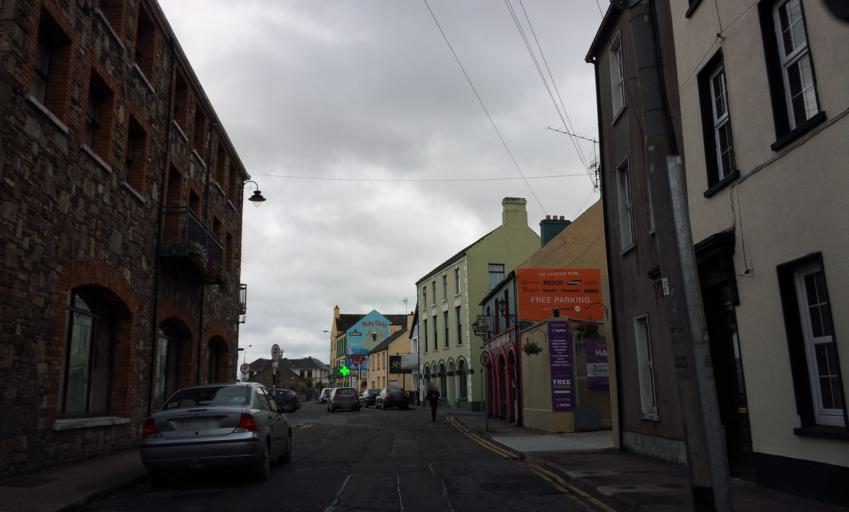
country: IE
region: Munster
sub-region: County Cork
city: Youghal
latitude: 51.9542
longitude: -7.8471
